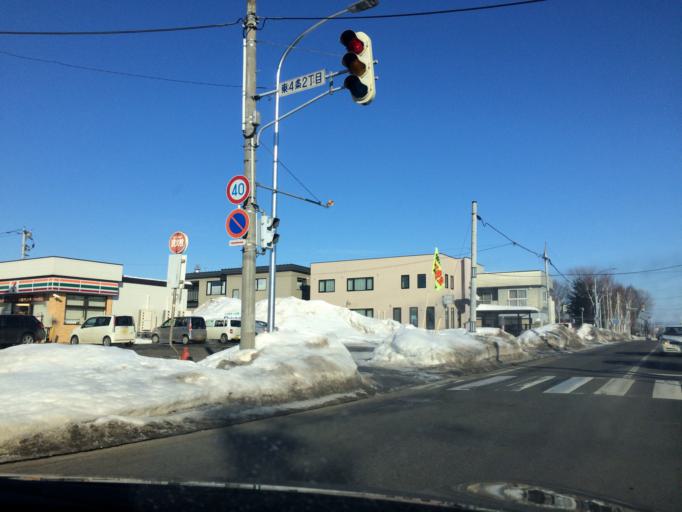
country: JP
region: Hokkaido
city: Obihiro
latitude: 42.9113
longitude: 143.0543
